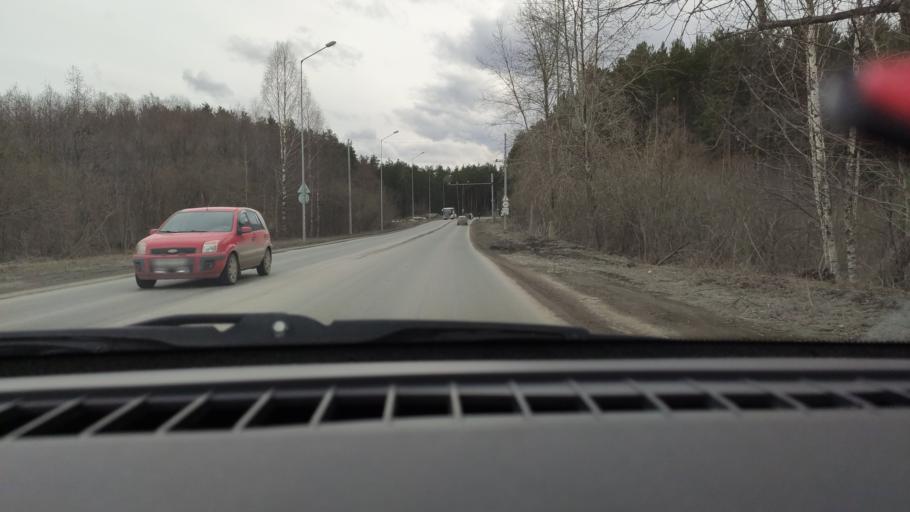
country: RU
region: Perm
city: Perm
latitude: 58.0806
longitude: 56.3087
